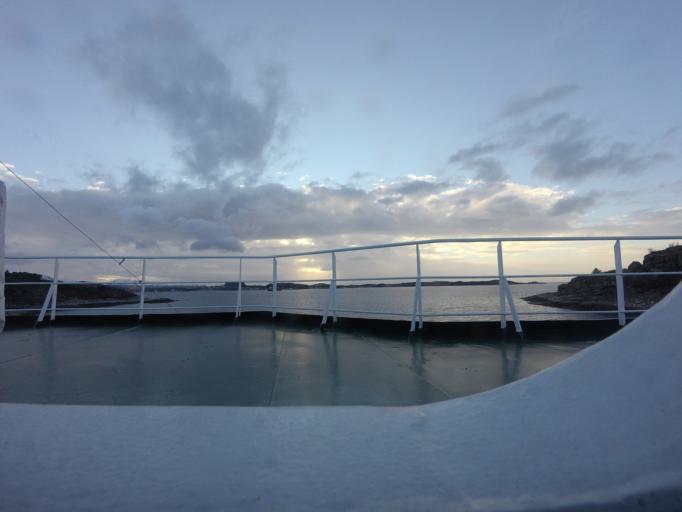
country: NO
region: More og Romsdal
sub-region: Kristiansund
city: Kristiansund
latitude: 63.1055
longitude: 7.7215
